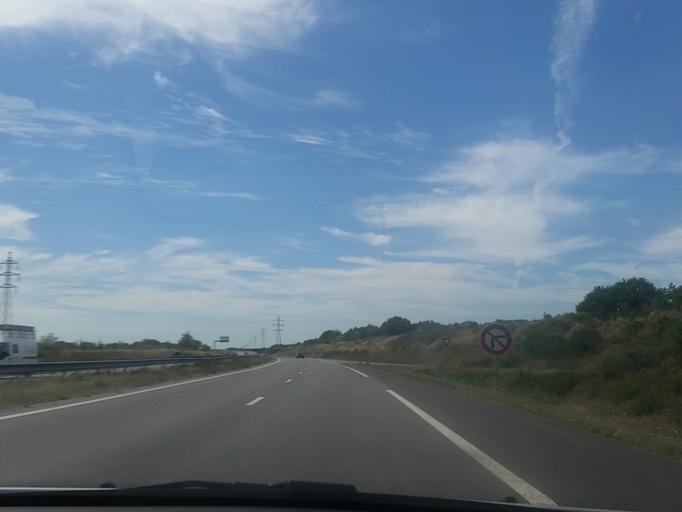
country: FR
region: Pays de la Loire
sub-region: Departement de la Loire-Atlantique
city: Saint-Jean-de-Boiseau
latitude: 47.1842
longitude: -1.7262
